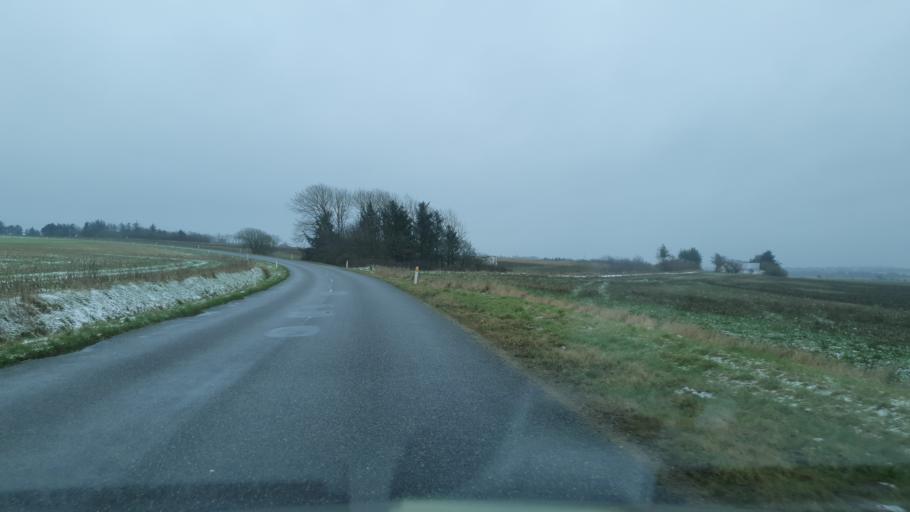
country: DK
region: North Denmark
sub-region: Jammerbugt Kommune
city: Brovst
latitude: 57.1285
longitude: 9.4731
